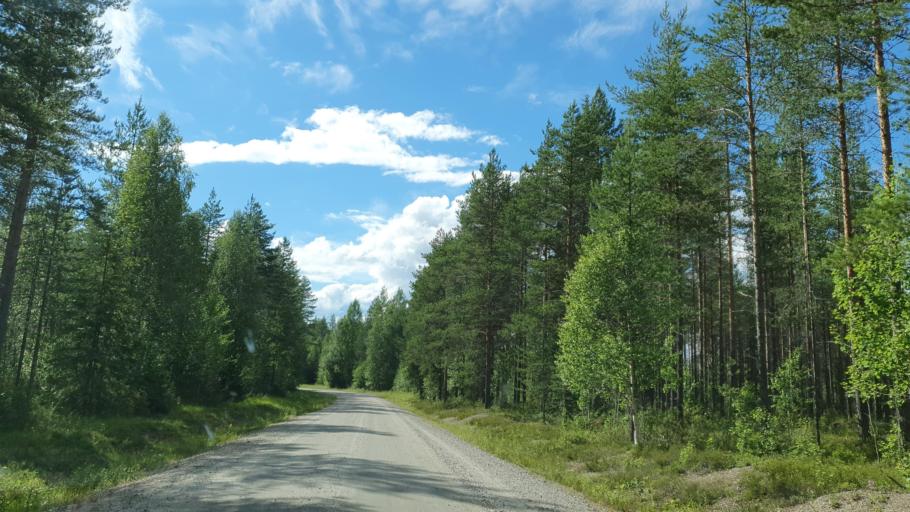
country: FI
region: Kainuu
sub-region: Kehys-Kainuu
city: Kuhmo
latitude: 64.1612
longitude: 29.8278
